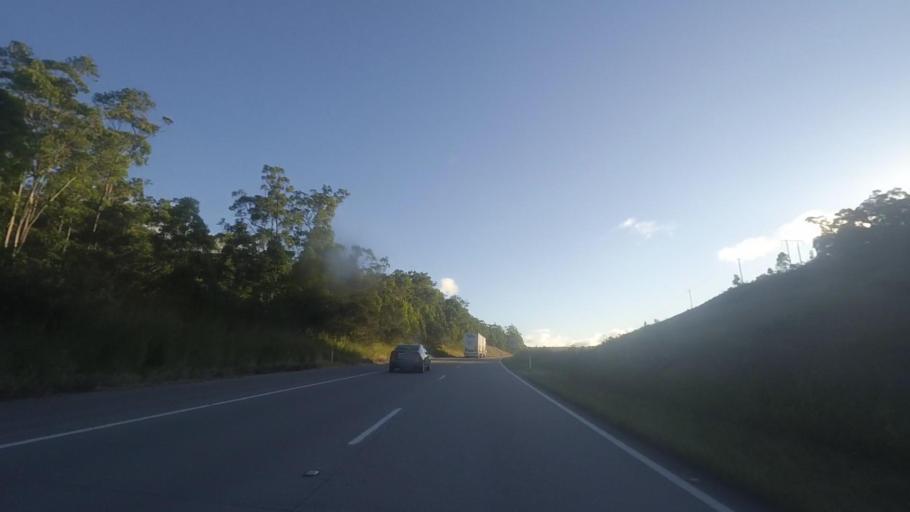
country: AU
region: New South Wales
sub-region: Great Lakes
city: Bulahdelah
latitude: -32.5146
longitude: 152.2097
